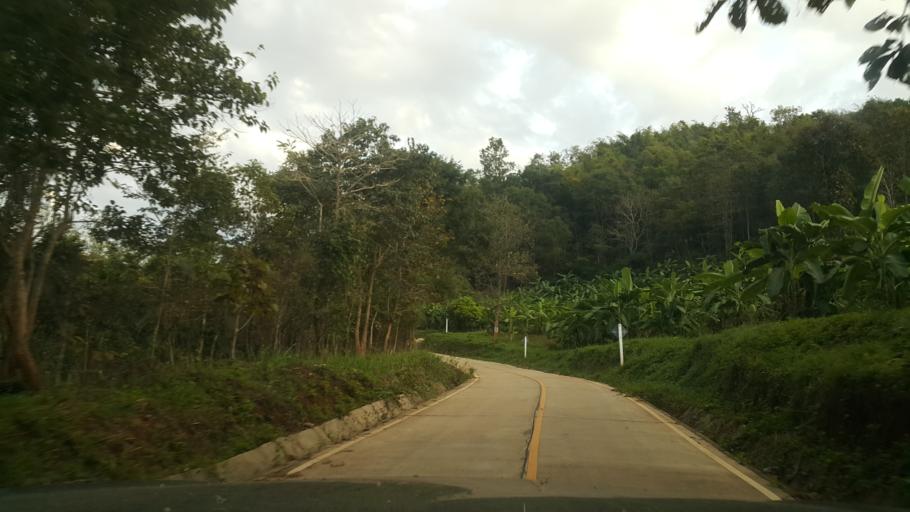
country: TH
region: Chiang Mai
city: Samoeng
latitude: 18.9952
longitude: 98.6742
